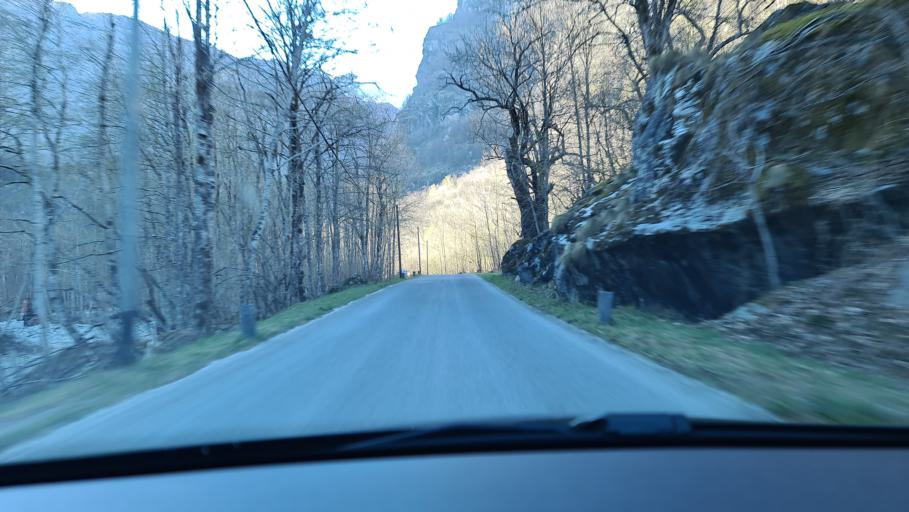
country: CH
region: Ticino
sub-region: Vallemaggia District
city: Cevio
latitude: 46.3692
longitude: 8.5608
